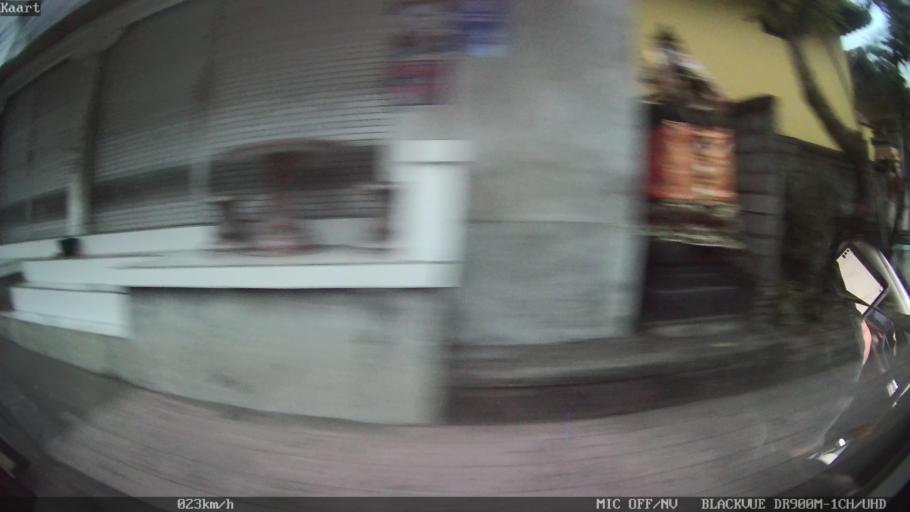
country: ID
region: Bali
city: Banjar Pasekan
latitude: -8.6292
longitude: 115.2845
